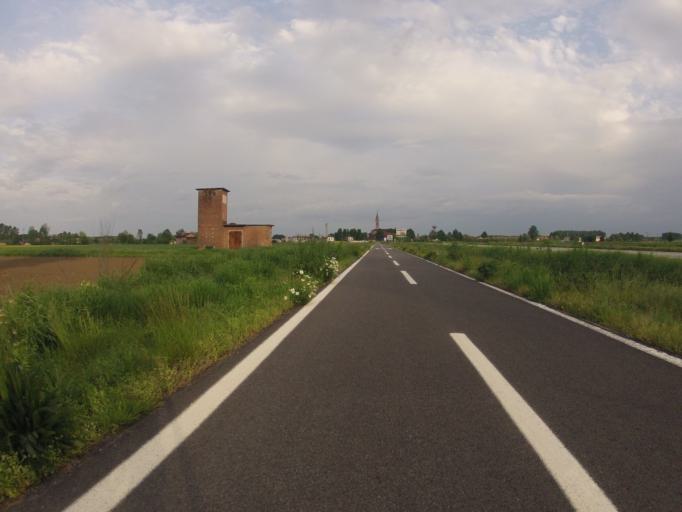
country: IT
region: Piedmont
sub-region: Provincia di Cuneo
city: Moretta
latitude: 44.7715
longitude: 7.5247
